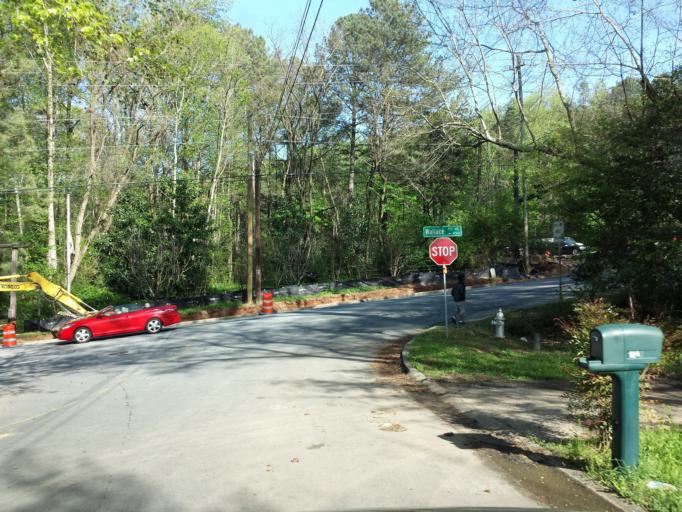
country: US
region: Georgia
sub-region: Cobb County
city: Marietta
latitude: 33.9628
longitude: -84.5141
